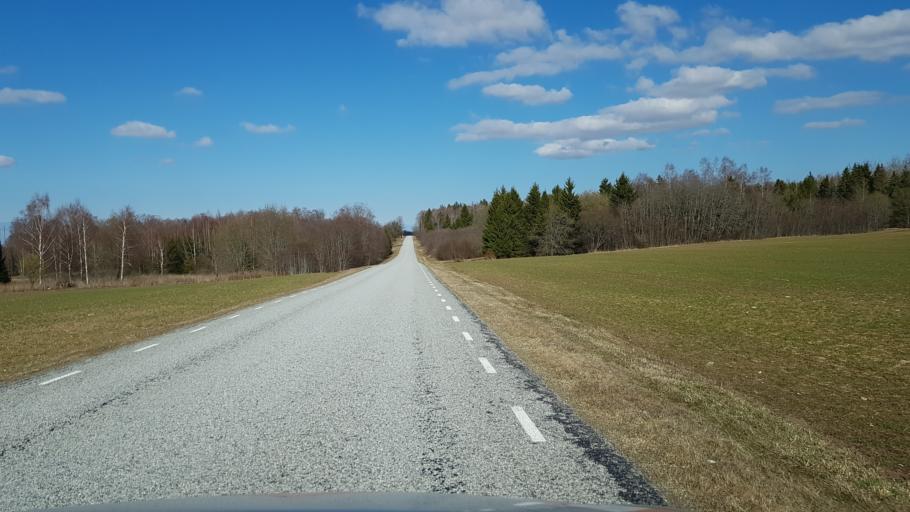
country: EE
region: Laeaene-Virumaa
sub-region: Kadrina vald
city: Kadrina
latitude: 59.3024
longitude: 26.2213
